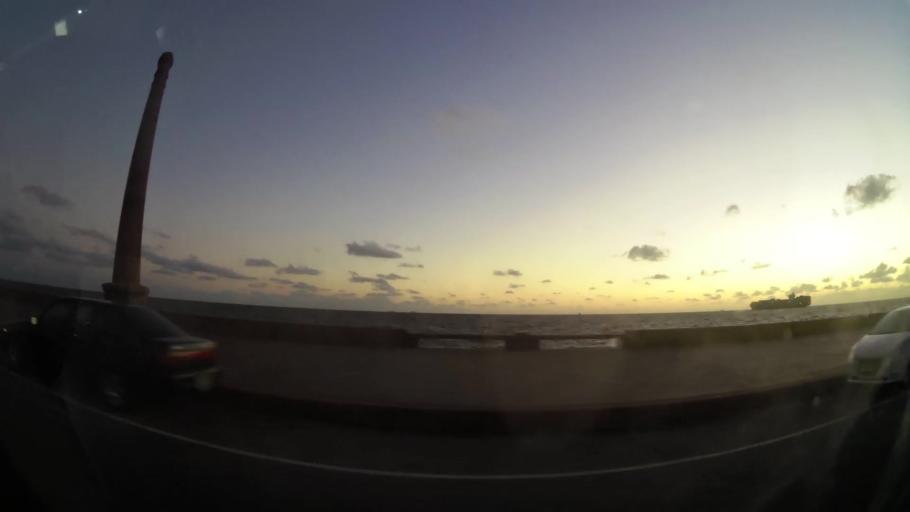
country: UY
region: Montevideo
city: Montevideo
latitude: -34.9118
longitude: -56.2110
